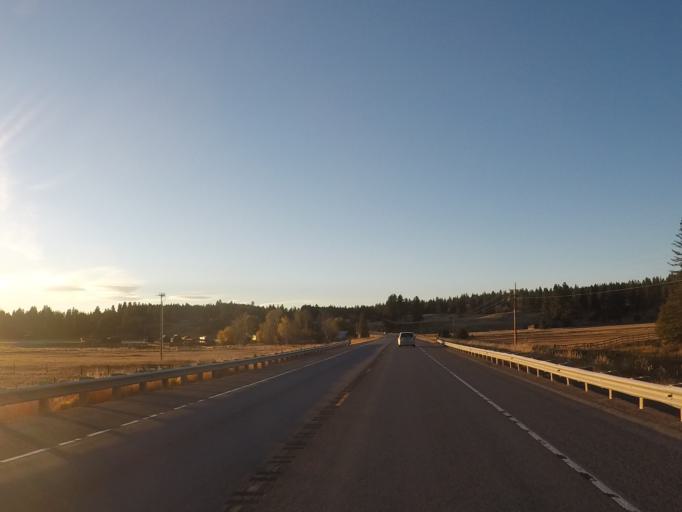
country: US
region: Montana
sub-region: Lewis and Clark County
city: Lincoln
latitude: 47.0050
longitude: -113.0456
